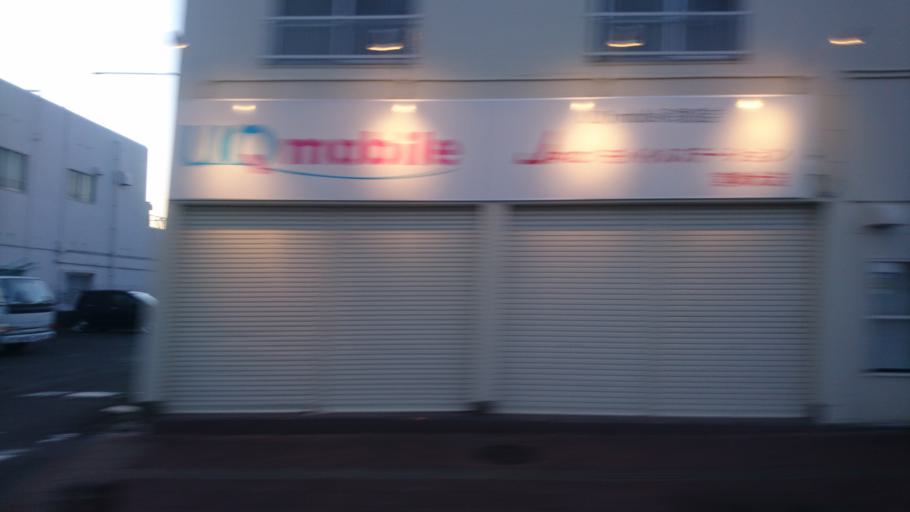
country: JP
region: Miyazaki
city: Miyazaki-shi
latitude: 31.8991
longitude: 131.4182
